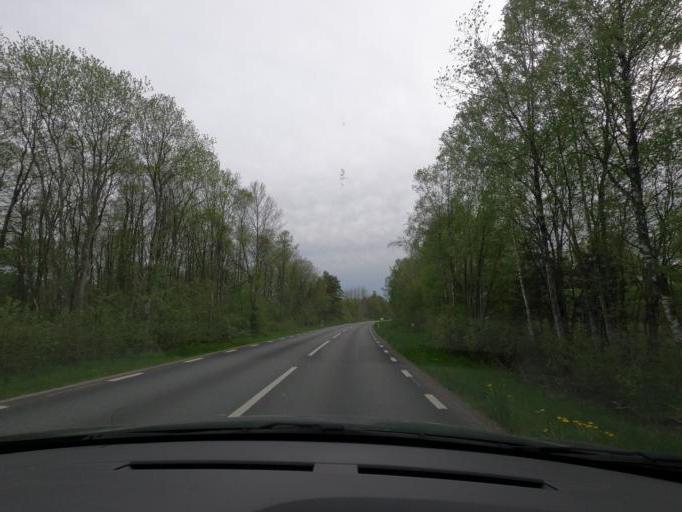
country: SE
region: Joenkoeping
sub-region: Varnamo Kommun
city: Bredaryd
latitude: 57.2175
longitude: 13.7771
